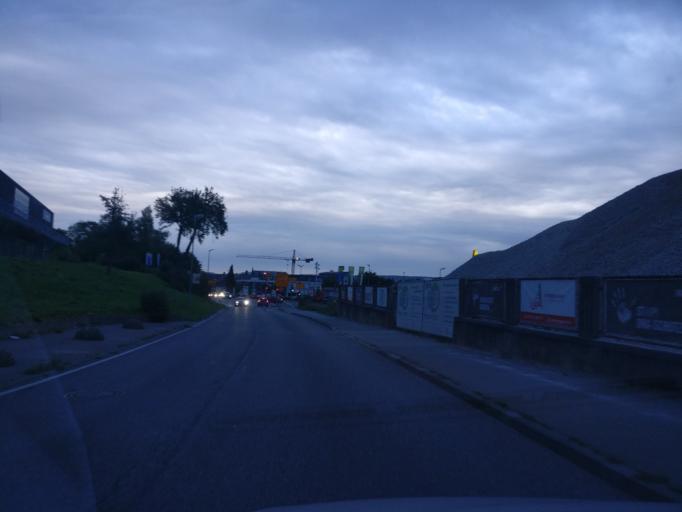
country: DE
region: Baden-Wuerttemberg
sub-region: Karlsruhe Region
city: Bretten
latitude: 49.0388
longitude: 8.6876
